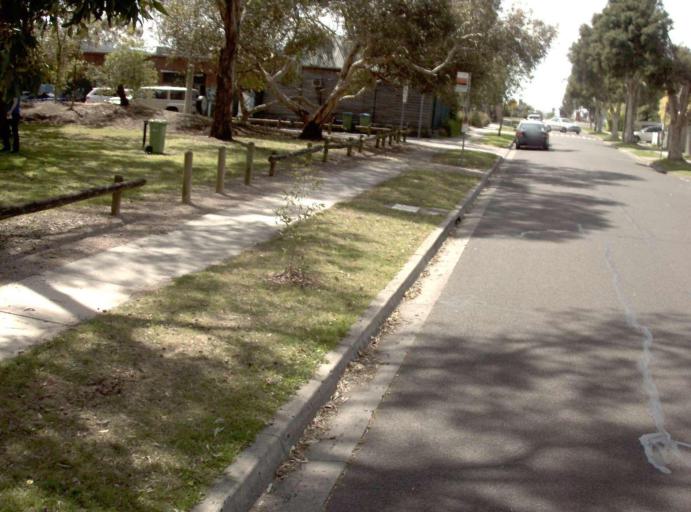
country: AU
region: Victoria
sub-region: Maroondah
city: Croydon Hills
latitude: -37.7844
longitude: 145.2694
